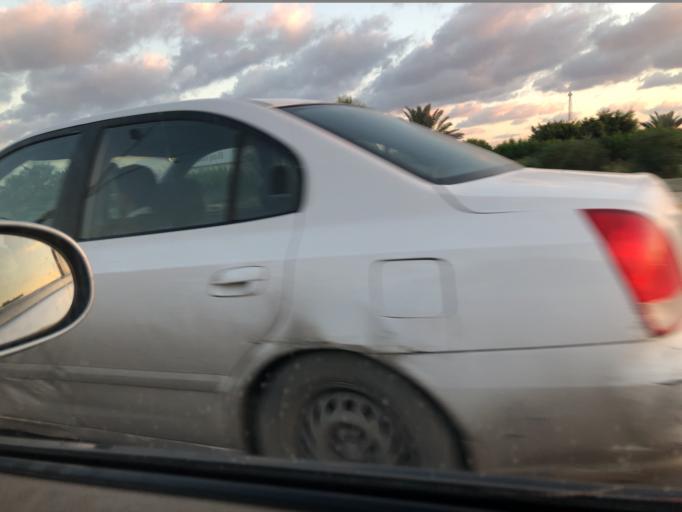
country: LY
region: Tripoli
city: Tripoli
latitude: 32.8992
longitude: 13.1780
